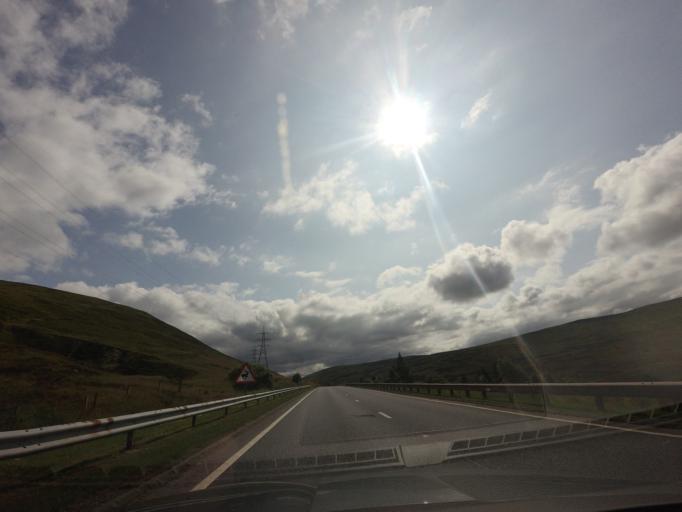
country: GB
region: Scotland
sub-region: Highland
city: Kingussie
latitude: 56.8207
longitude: -4.1851
